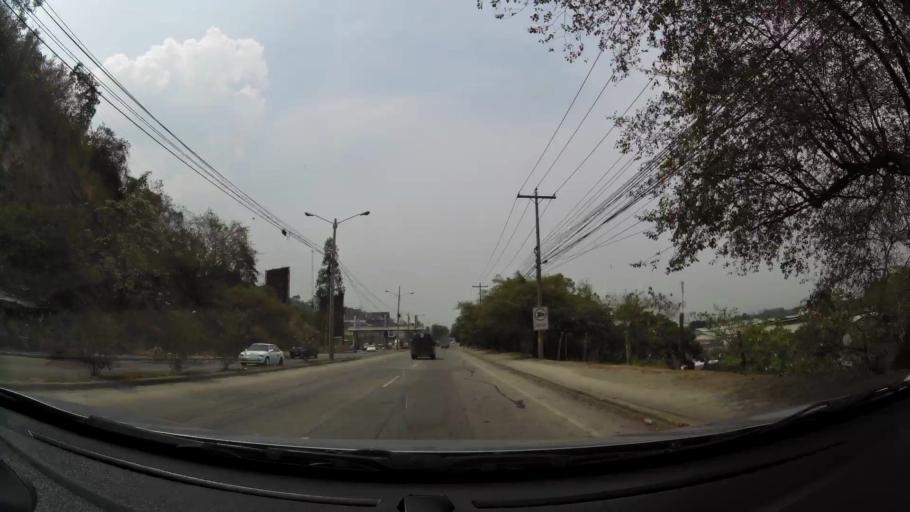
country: HN
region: Cortes
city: Chotepe
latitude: 15.4362
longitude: -88.0209
